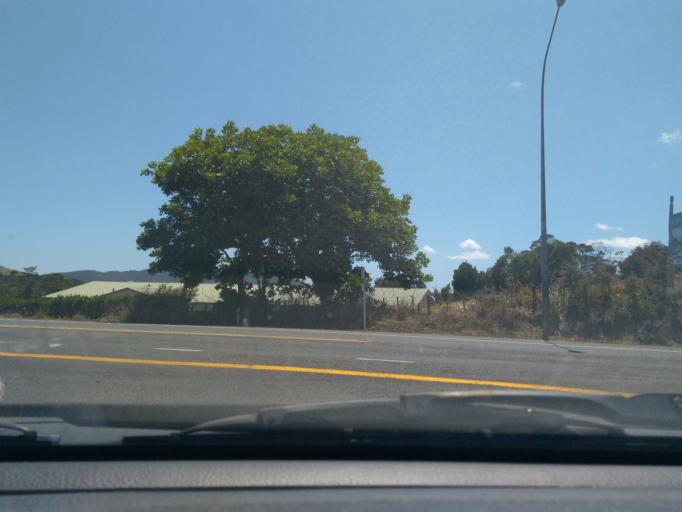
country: NZ
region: Northland
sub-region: Far North District
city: Taipa
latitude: -34.9917
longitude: 173.5231
